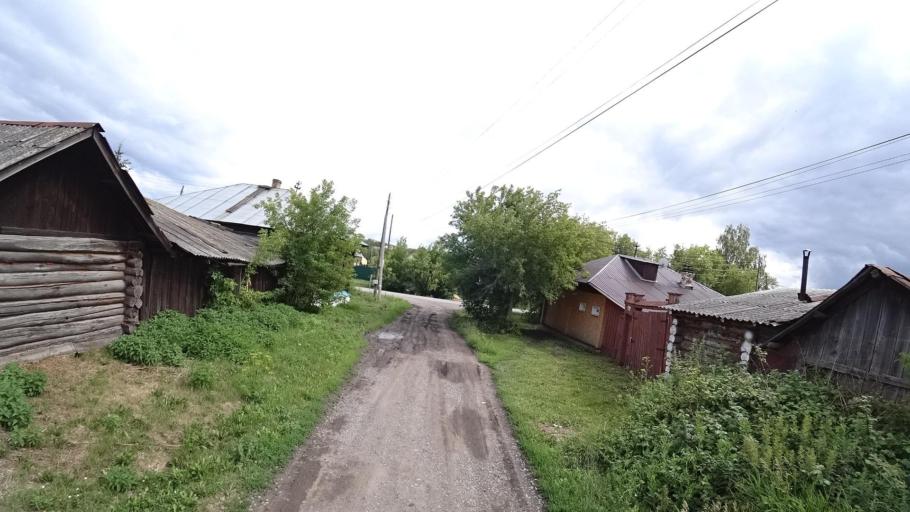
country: RU
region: Sverdlovsk
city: Kamyshlov
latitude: 56.8542
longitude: 62.6987
